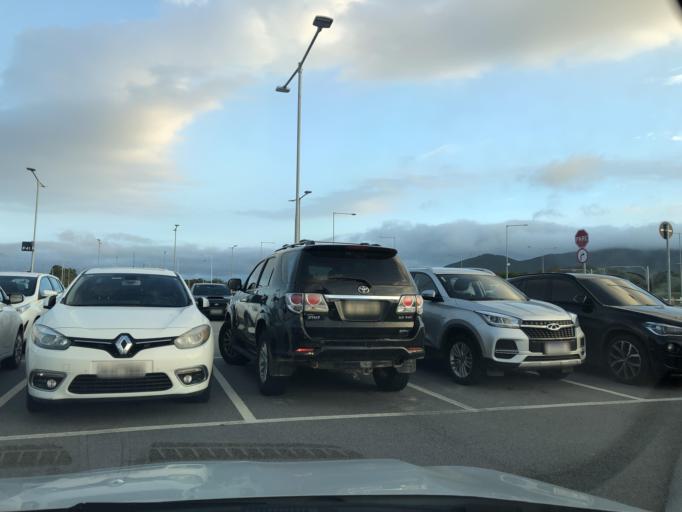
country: BR
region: Santa Catarina
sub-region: Florianopolis
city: Tapera
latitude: -27.6760
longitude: -48.5456
